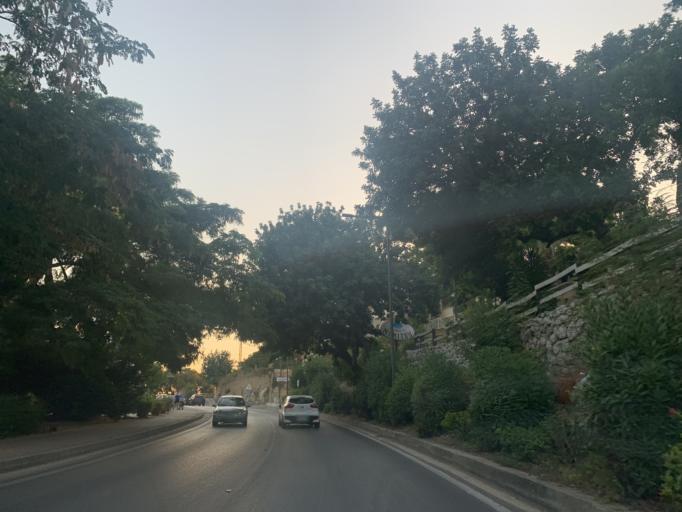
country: LB
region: Mont-Liban
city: Djounie
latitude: 33.9616
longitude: 35.6277
